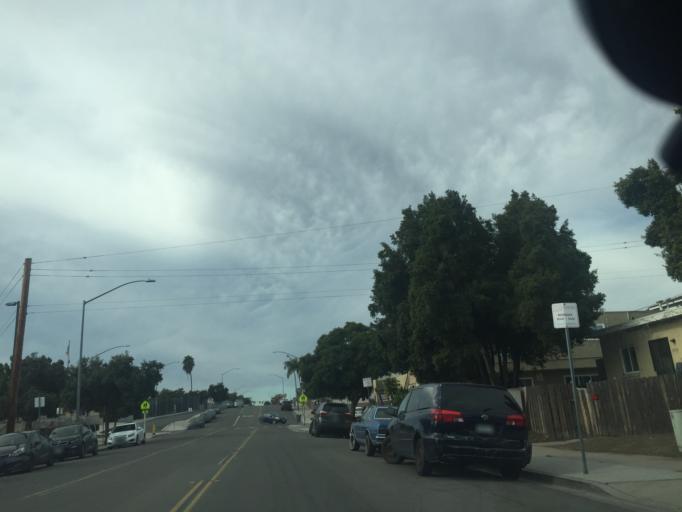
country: US
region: California
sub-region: San Diego County
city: Lemon Grove
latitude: 32.7531
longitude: -117.0882
